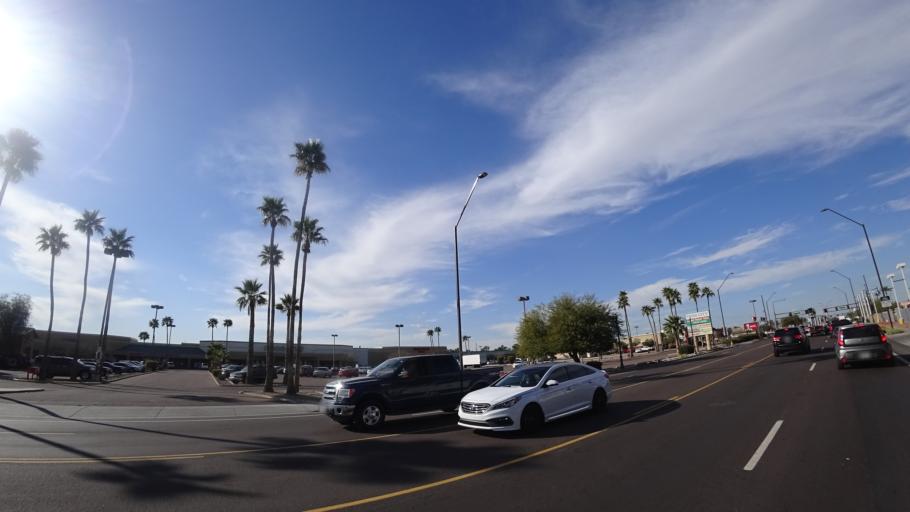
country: US
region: Arizona
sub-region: Maricopa County
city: Avondale
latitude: 33.4482
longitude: -112.3410
